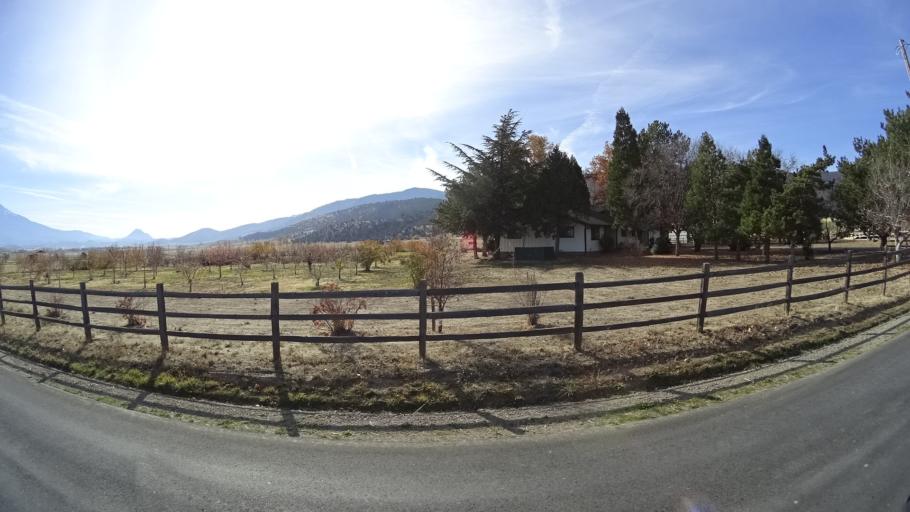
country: US
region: California
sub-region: Siskiyou County
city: Montague
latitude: 41.5381
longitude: -122.5480
